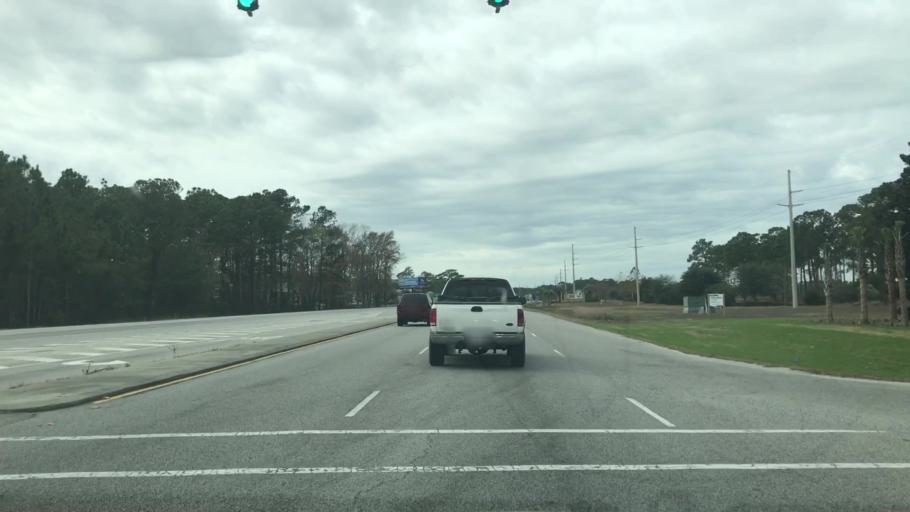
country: US
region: South Carolina
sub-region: Horry County
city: Myrtle Beach
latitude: 33.7641
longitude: -78.8118
